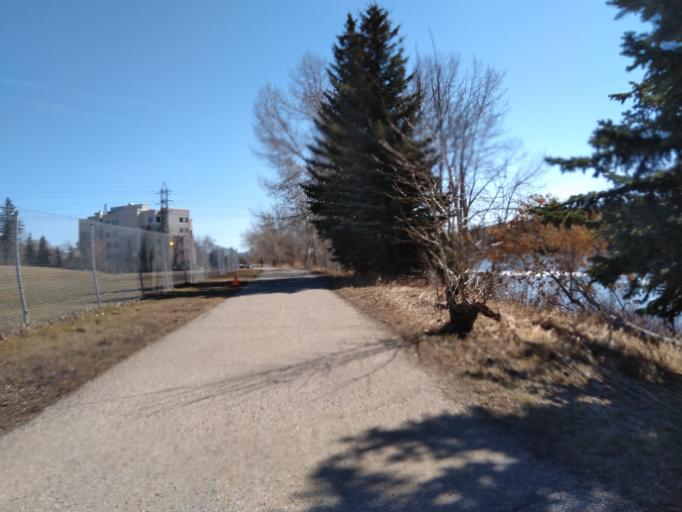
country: CA
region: Alberta
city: Calgary
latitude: 51.0687
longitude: -114.1663
